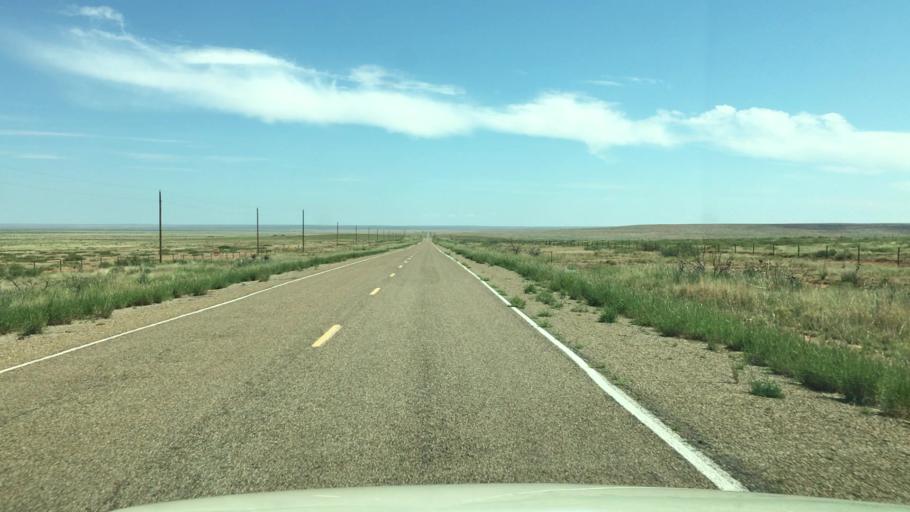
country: US
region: New Mexico
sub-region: De Baca County
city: Fort Sumner
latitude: 33.9900
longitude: -104.5707
